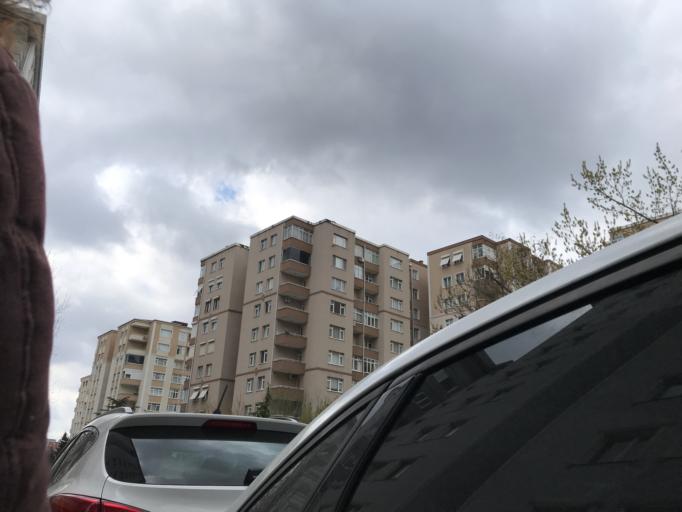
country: TR
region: Istanbul
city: Maltepe
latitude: 40.9386
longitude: 29.1378
